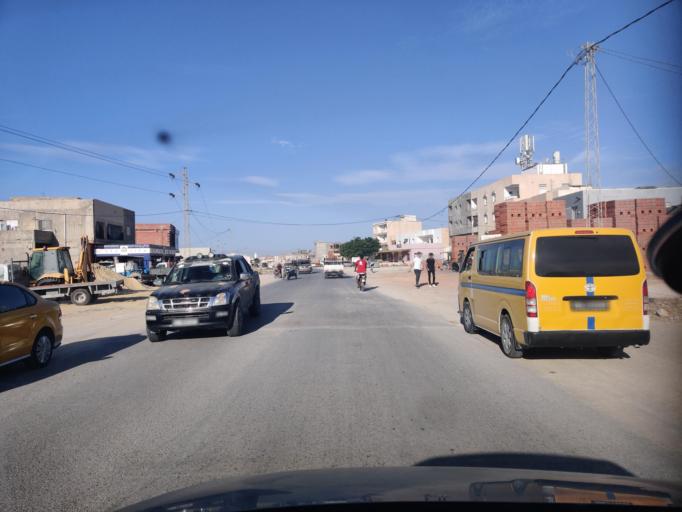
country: TN
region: Ariana
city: Ariana
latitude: 36.9571
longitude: 10.2067
